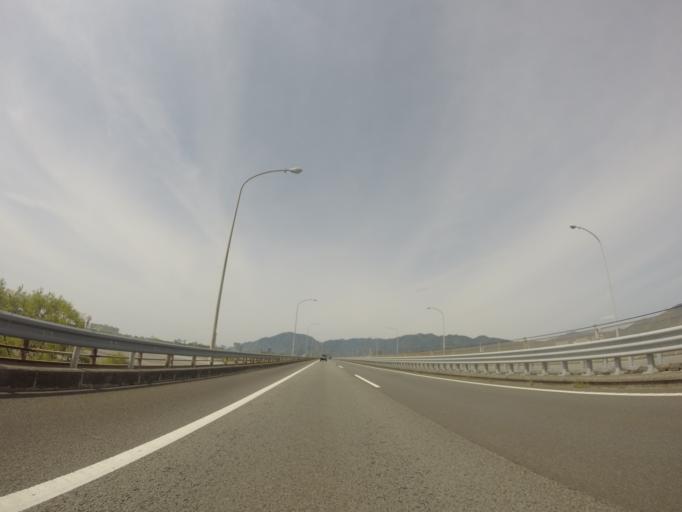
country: JP
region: Shizuoka
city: Shizuoka-shi
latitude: 34.9432
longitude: 138.3870
